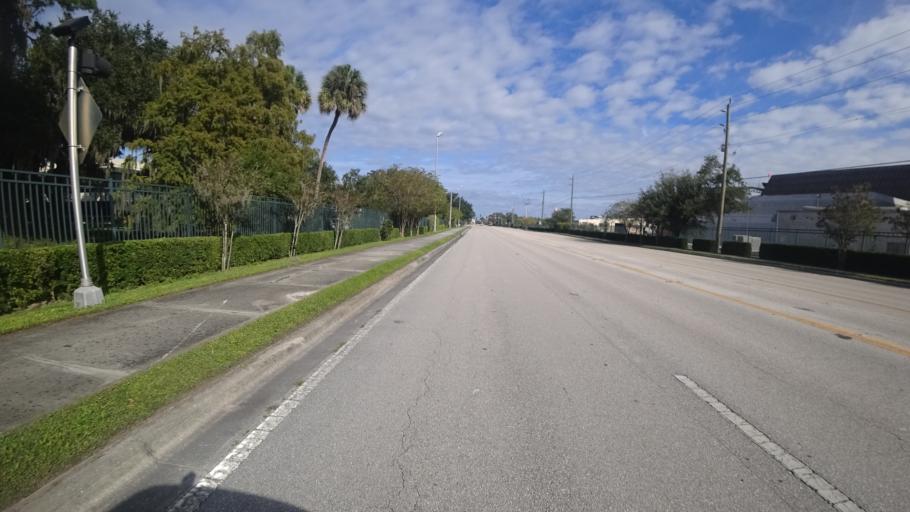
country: US
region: Florida
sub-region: Manatee County
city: West Samoset
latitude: 27.4860
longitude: -82.5549
